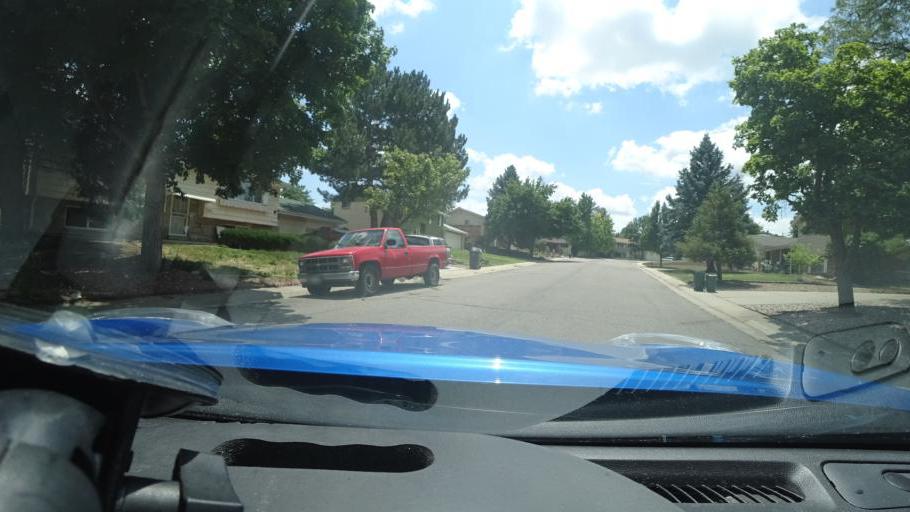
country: US
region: Colorado
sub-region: Adams County
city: Aurora
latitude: 39.7105
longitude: -104.8397
